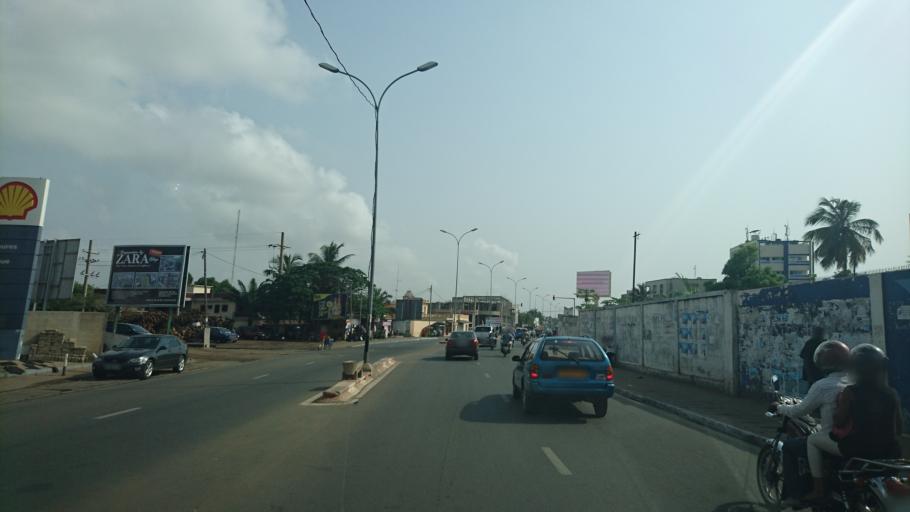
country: TG
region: Maritime
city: Lome
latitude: 6.1353
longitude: 1.2177
